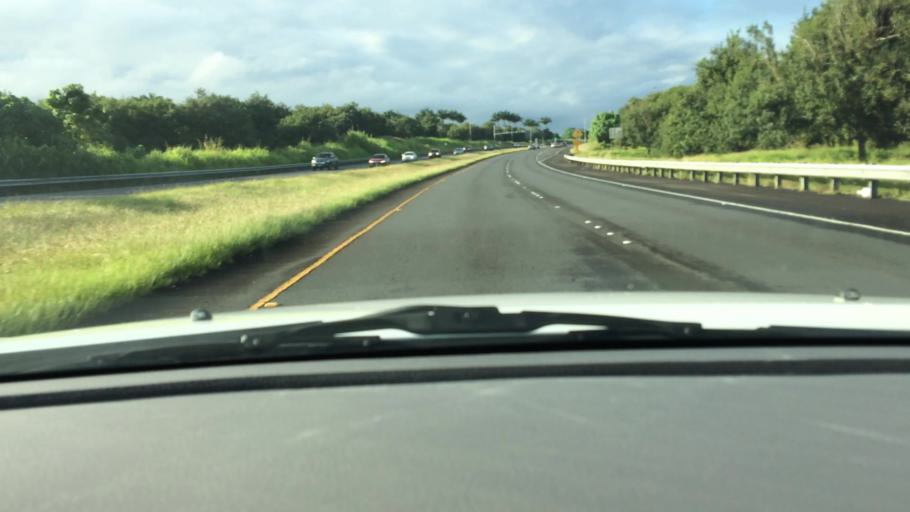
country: US
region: Hawaii
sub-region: Hawaii County
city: Kea'au
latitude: 19.6199
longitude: -155.0306
